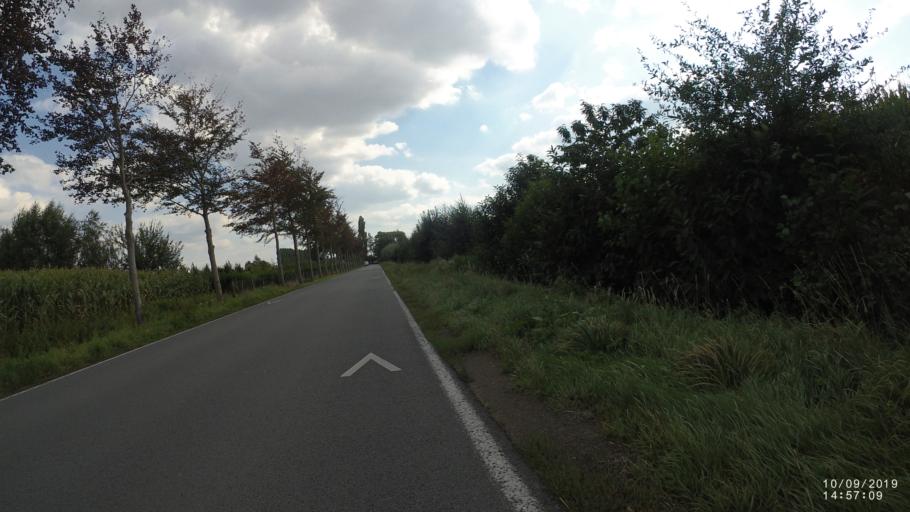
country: BE
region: Flanders
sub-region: Provincie Oost-Vlaanderen
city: Evergem
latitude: 51.1345
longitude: 3.7042
